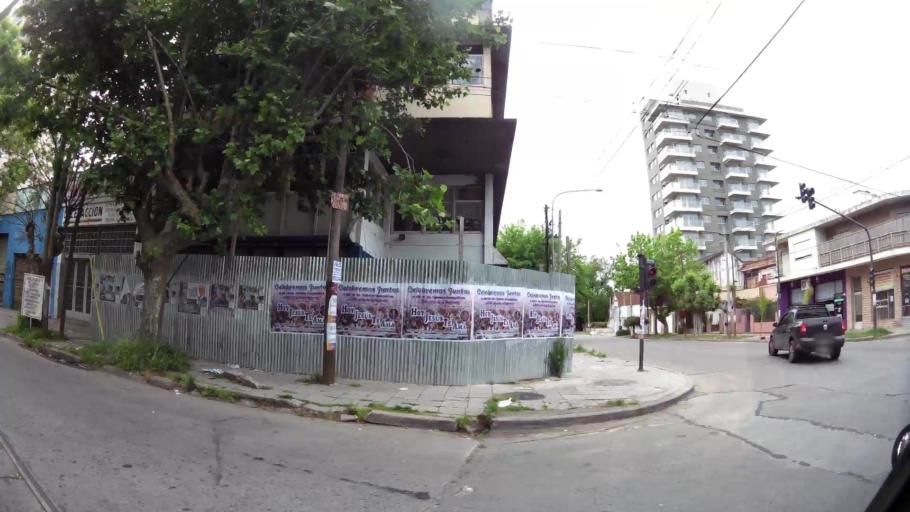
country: AR
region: Buenos Aires
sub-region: Partido de Quilmes
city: Quilmes
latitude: -34.7282
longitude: -58.2566
